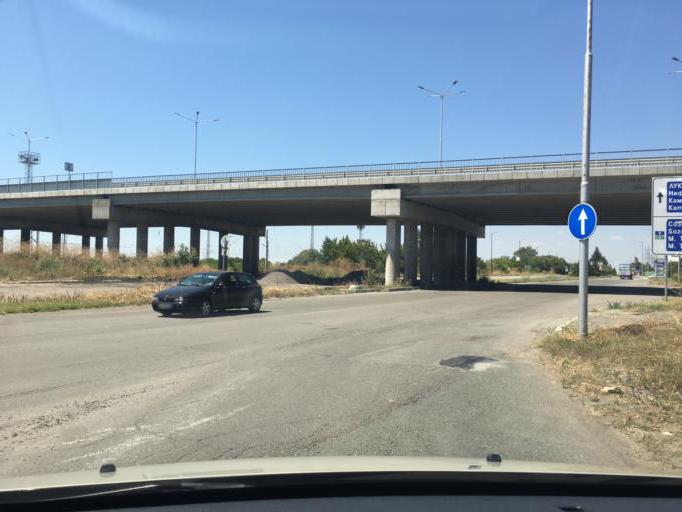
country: BG
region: Burgas
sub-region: Obshtina Burgas
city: Burgas
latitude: 42.5154
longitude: 27.4373
